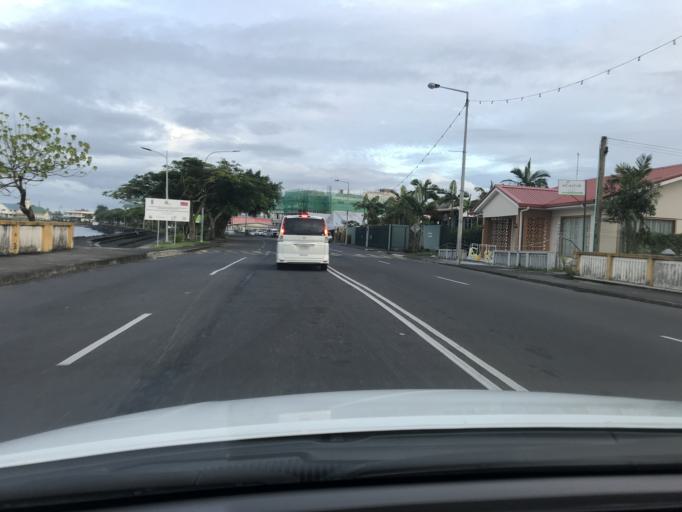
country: WS
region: Tuamasaga
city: Apia
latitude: -13.8319
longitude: -171.7659
